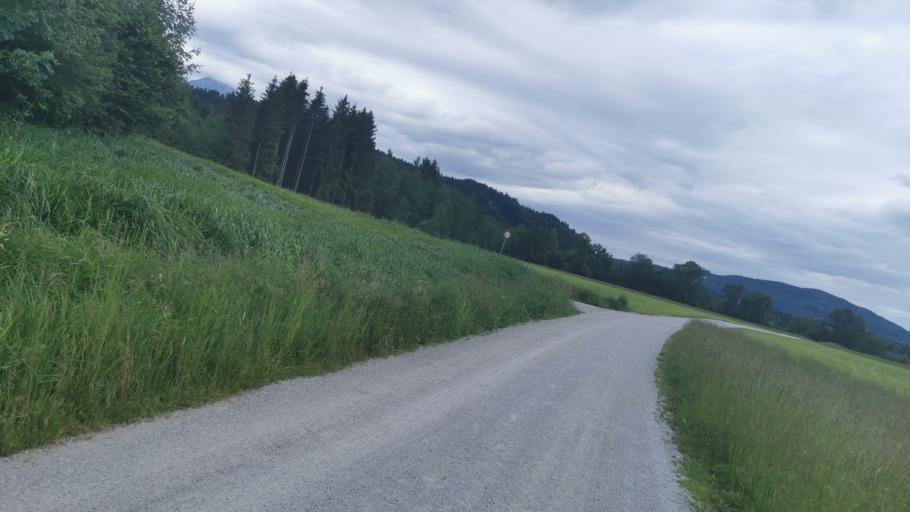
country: DE
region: Bavaria
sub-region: Upper Bavaria
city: Piding
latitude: 47.7595
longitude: 12.9731
